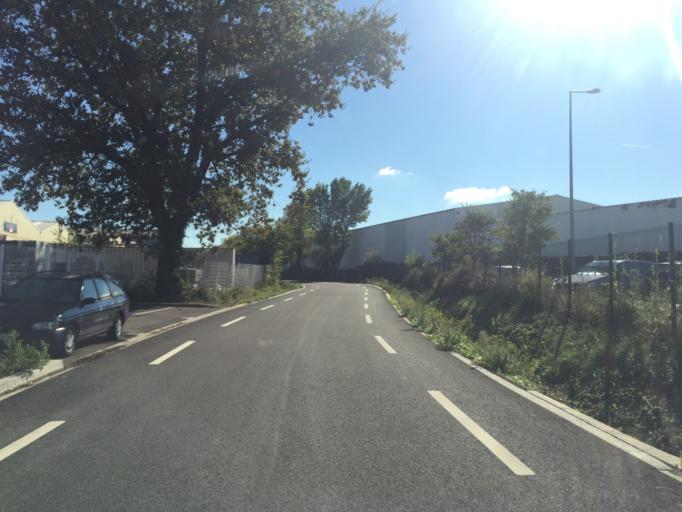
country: FR
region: Provence-Alpes-Cote d'Azur
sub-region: Departement du Vaucluse
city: Avignon
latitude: 43.9382
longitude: 4.8363
